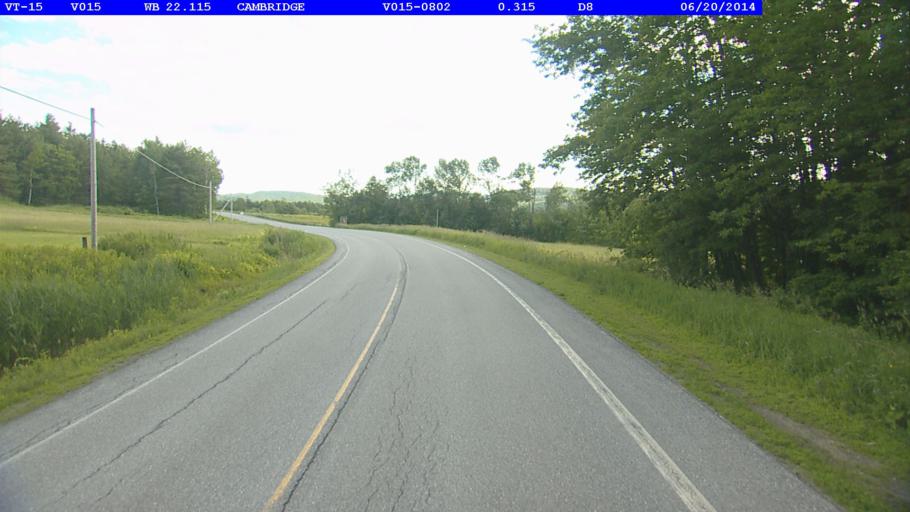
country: US
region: Vermont
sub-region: Chittenden County
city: Jericho
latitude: 44.6356
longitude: -72.9130
